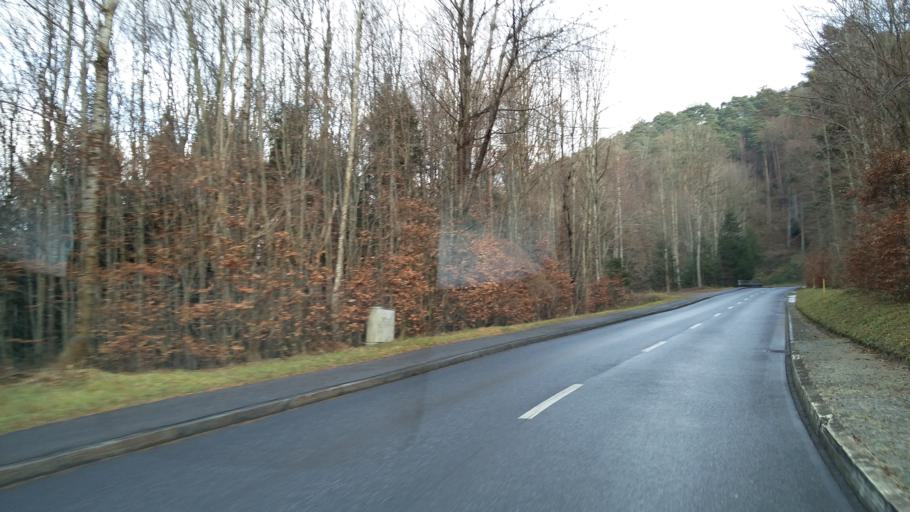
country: LI
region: Planken
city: Planken
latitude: 47.1765
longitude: 9.5356
